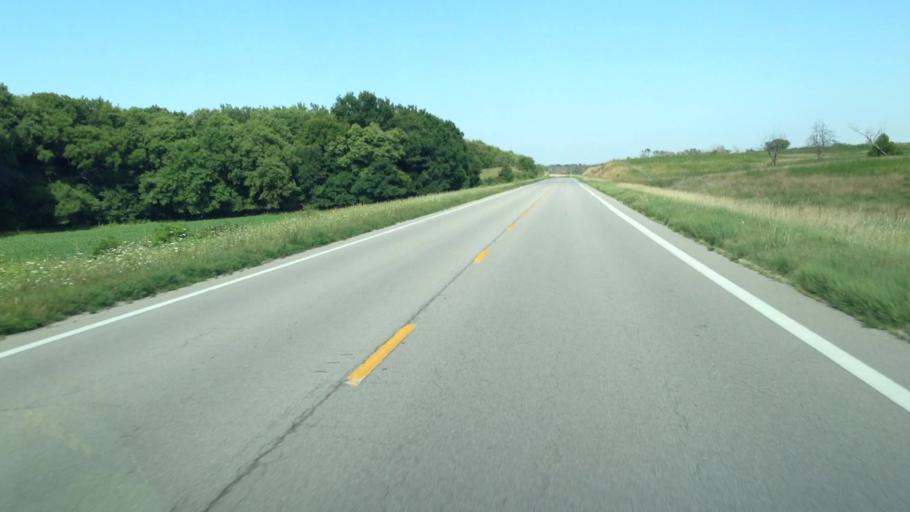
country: US
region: Kansas
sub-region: Neosho County
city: Erie
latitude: 37.6888
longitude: -95.1779
